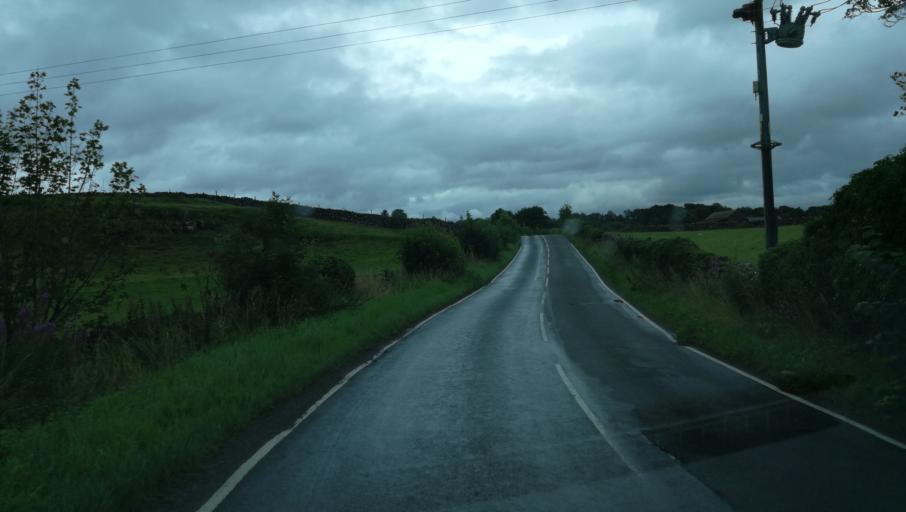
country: GB
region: England
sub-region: Cumbria
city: Penrith
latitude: 54.6407
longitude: -2.7920
